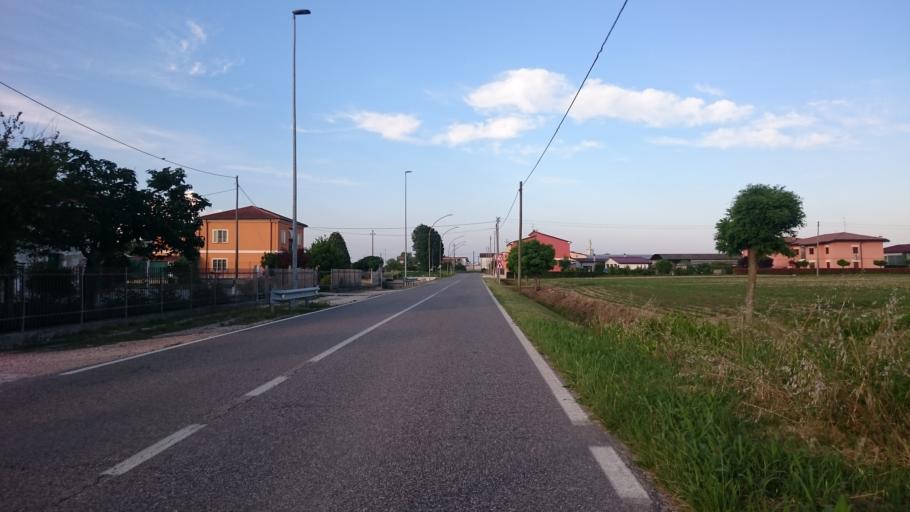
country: IT
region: Veneto
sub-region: Provincia di Verona
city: Casaleone
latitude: 45.1527
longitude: 11.1814
